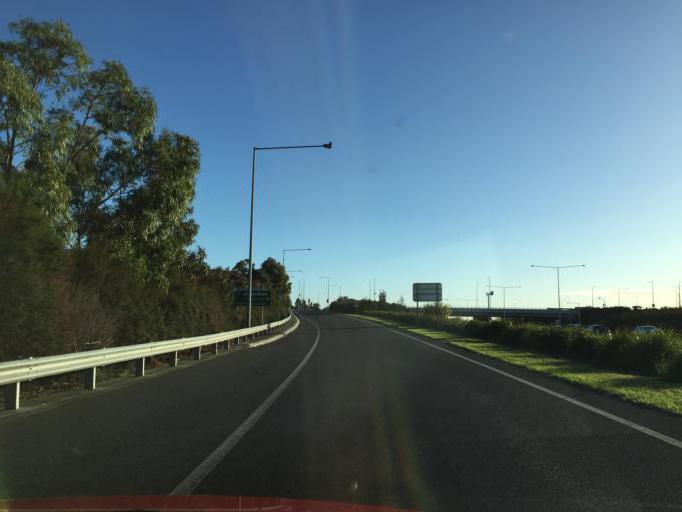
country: AU
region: Victoria
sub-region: Frankston
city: Sandhurst
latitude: -38.0727
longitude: 145.1811
